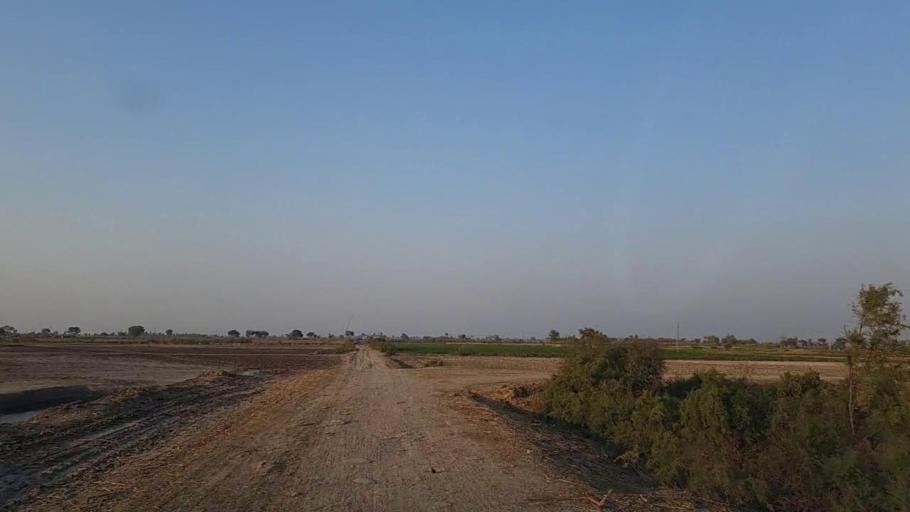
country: PK
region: Sindh
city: Bandhi
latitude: 26.5481
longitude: 68.3167
